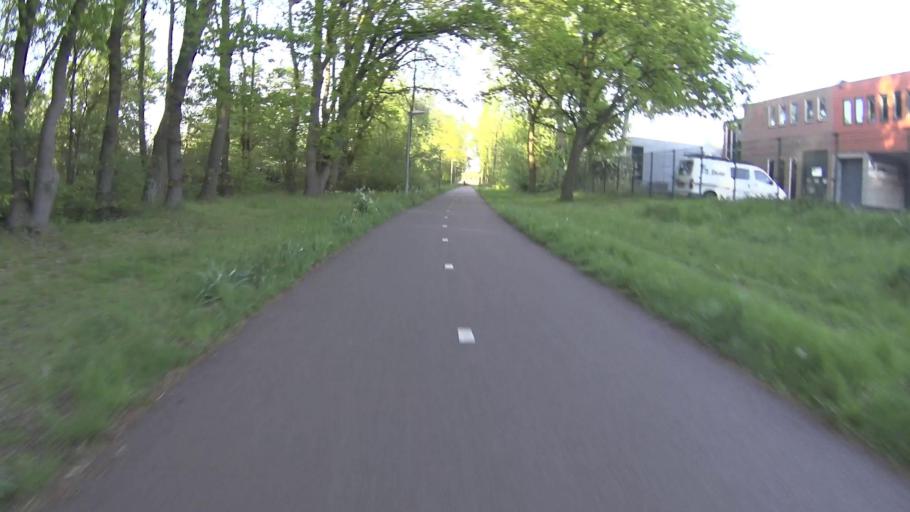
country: NL
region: South Holland
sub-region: Gemeente Wassenaar
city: Wassenaar
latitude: 52.1511
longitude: 4.4313
